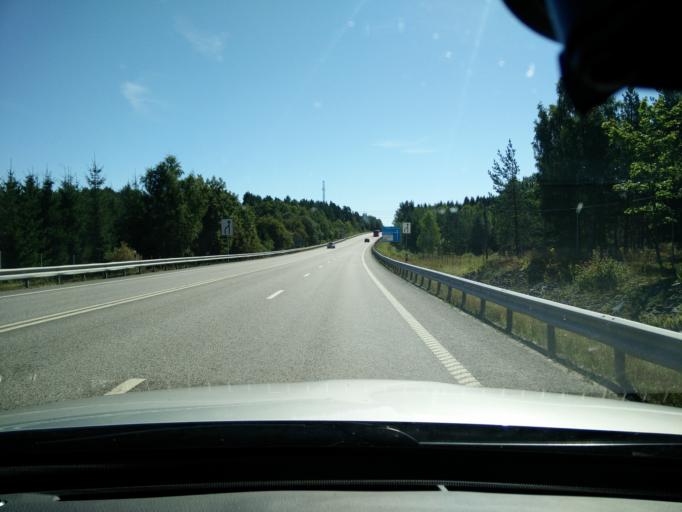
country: SE
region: Stockholm
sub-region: Osterakers Kommun
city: Akersberga
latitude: 59.4524
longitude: 18.2073
